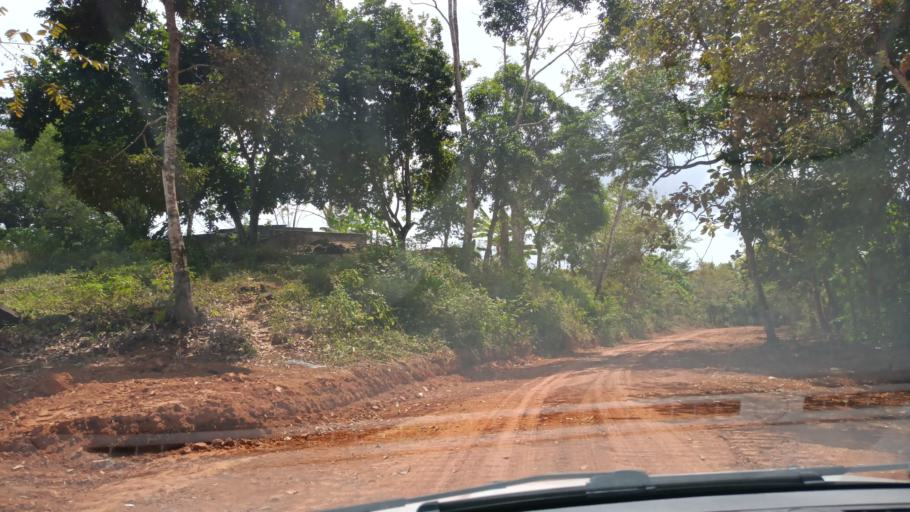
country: PA
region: Panama
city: La Cabima
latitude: 9.1215
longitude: -79.4949
